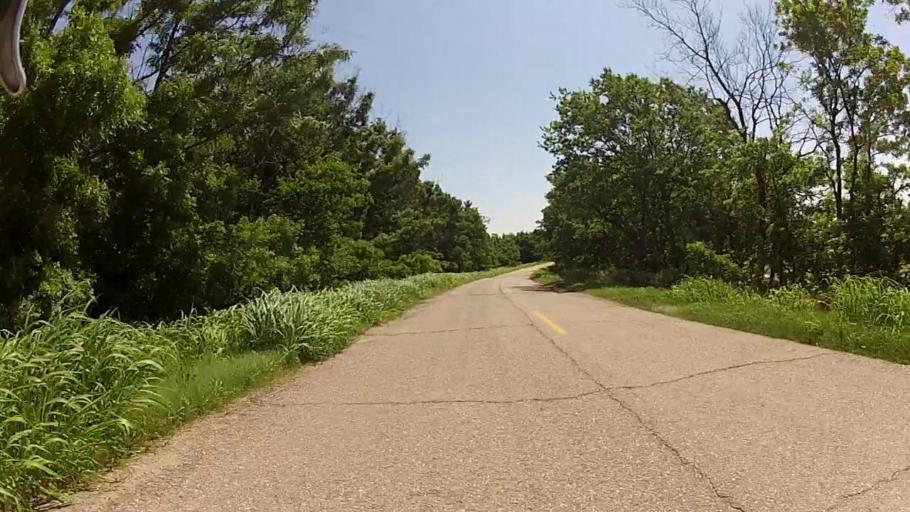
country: US
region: Kansas
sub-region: Sumner County
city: Caldwell
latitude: 37.0339
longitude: -97.4914
